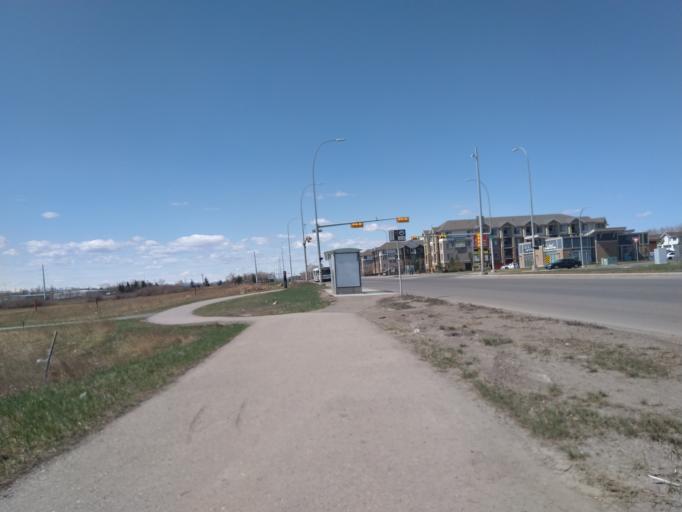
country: CA
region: Alberta
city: Chestermere
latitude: 51.0377
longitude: -113.9293
